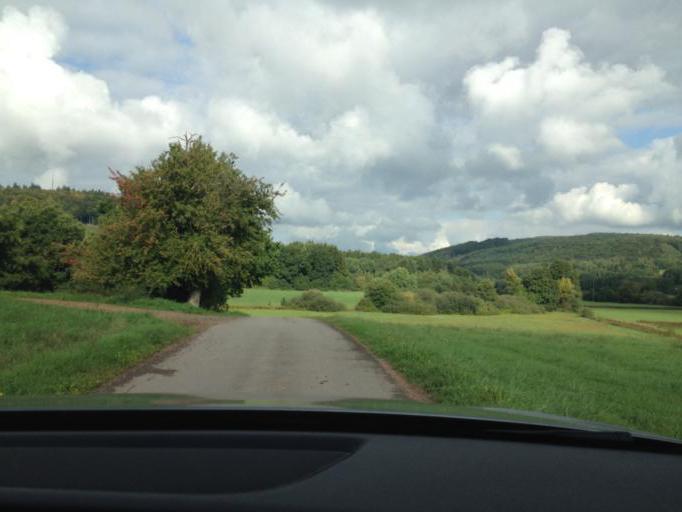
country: DE
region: Saarland
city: Nohfelden
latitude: 49.5679
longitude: 7.1677
